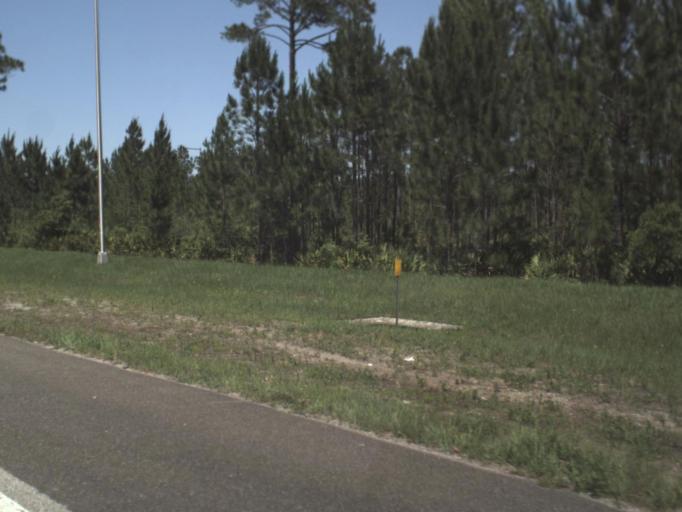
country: US
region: Florida
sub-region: Clay County
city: Bellair-Meadowbrook Terrace
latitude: 30.2060
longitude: -81.8372
